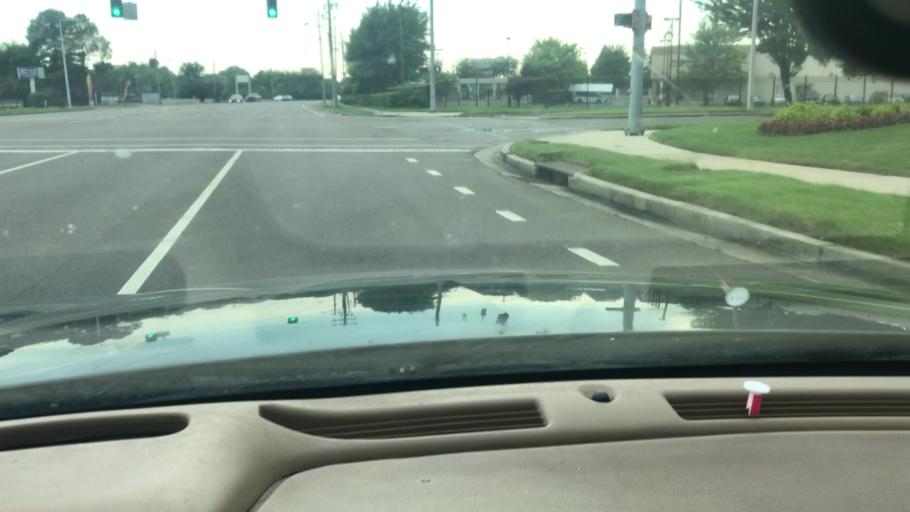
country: US
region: Tennessee
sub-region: Shelby County
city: Germantown
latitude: 35.0748
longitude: -89.9015
